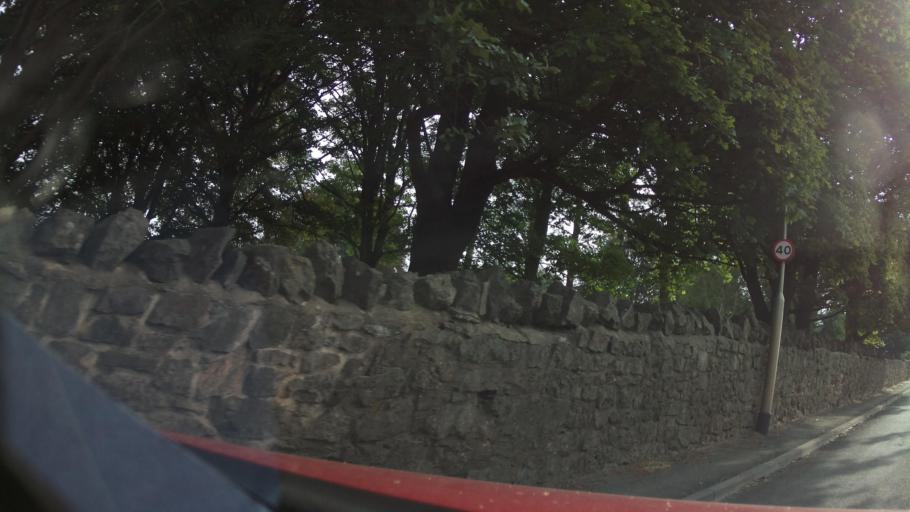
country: GB
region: England
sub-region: North Somerset
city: Long Ashton
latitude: 51.4245
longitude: -2.6938
